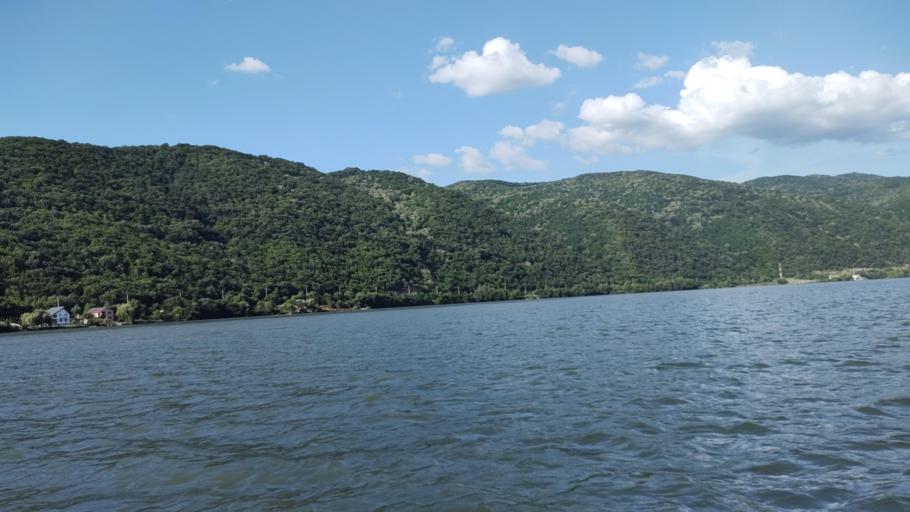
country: RO
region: Caras-Severin
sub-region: Comuna Berzasca
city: Berzasca
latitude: 44.6346
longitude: 21.9776
